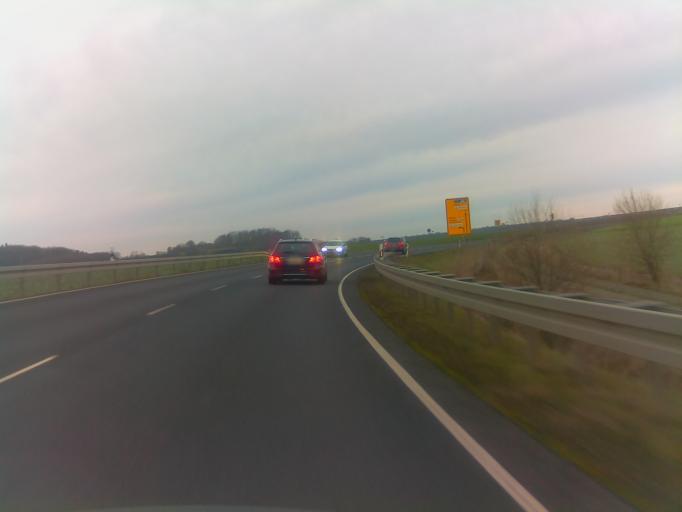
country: DE
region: Hesse
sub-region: Regierungsbezirk Kassel
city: Hunfeld
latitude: 50.6918
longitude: 9.7910
